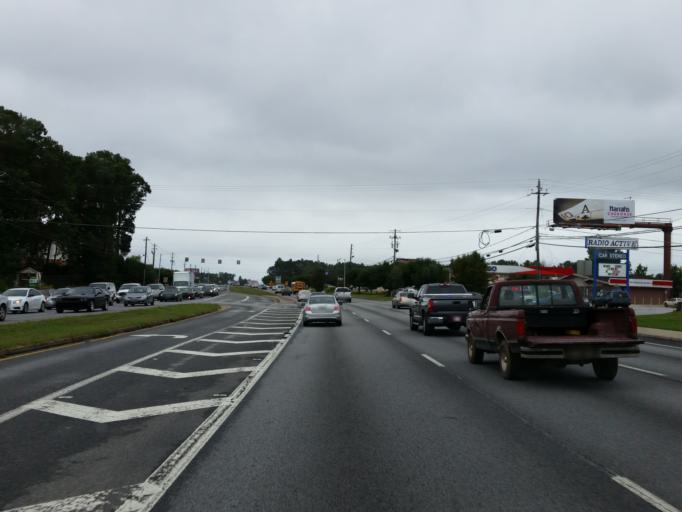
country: US
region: Georgia
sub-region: Clayton County
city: Morrow
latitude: 33.5707
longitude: -84.3720
